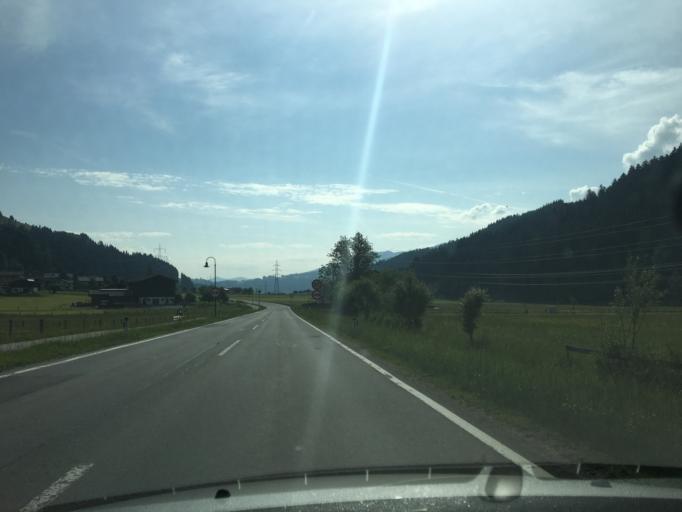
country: AT
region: Salzburg
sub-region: Politischer Bezirk Sankt Johann im Pongau
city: Wagrain
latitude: 47.3565
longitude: 13.3344
